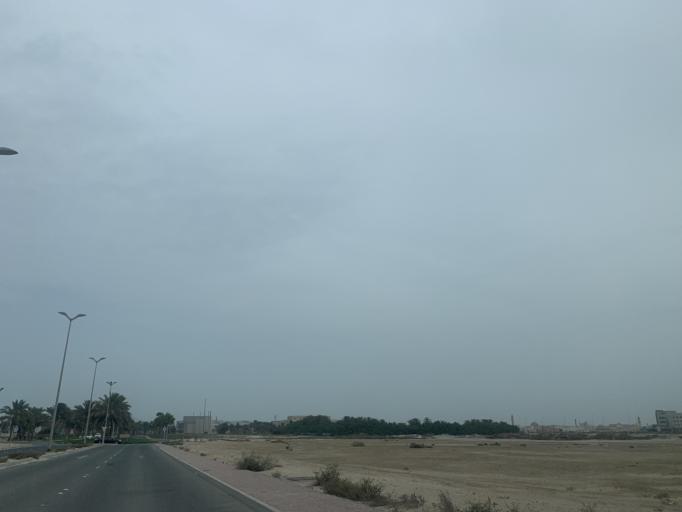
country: BH
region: Muharraq
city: Al Hadd
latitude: 26.2824
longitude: 50.6563
